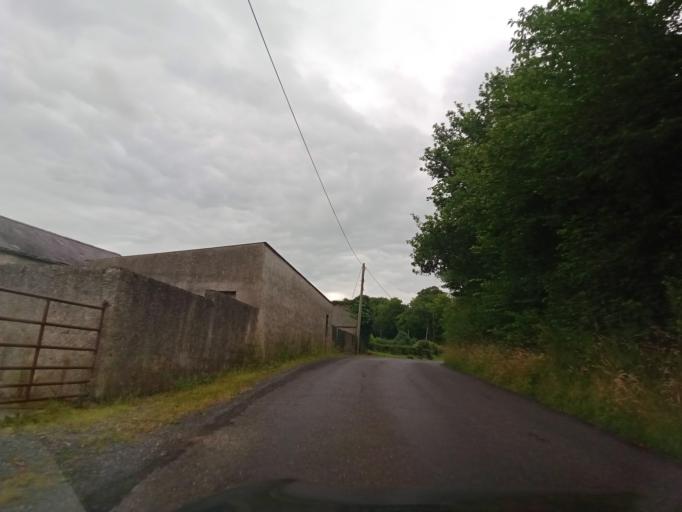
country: IE
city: Ballylinan
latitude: 52.9222
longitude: -7.0721
